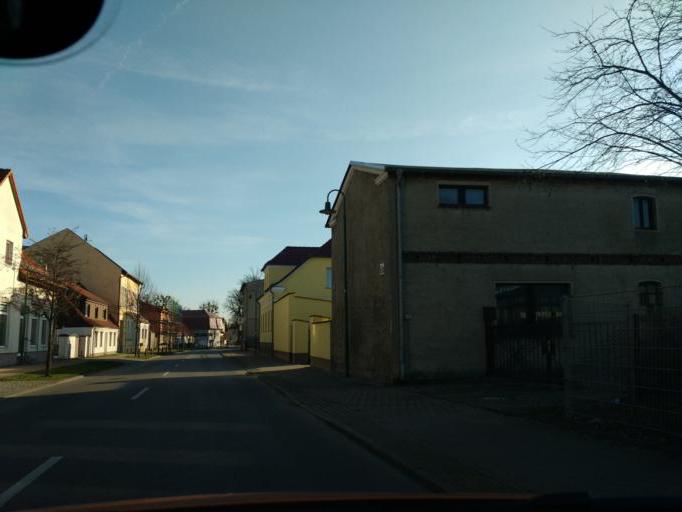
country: DE
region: Brandenburg
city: Werneuchen
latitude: 52.6313
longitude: 13.7292
